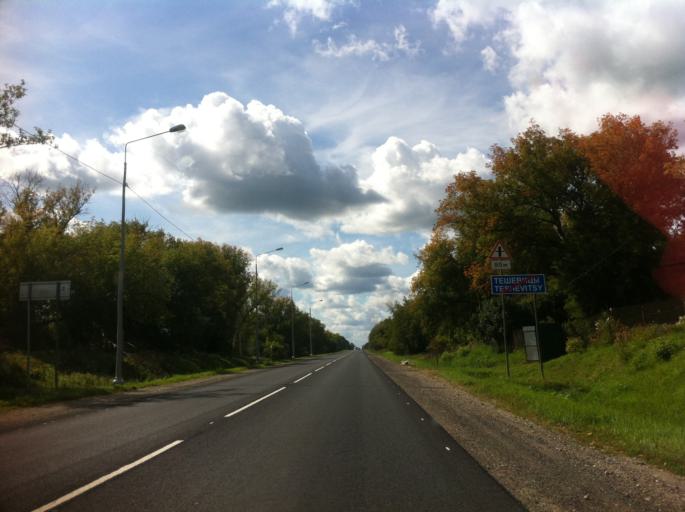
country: RU
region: Pskov
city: Izborsk
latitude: 57.7303
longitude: 27.9714
